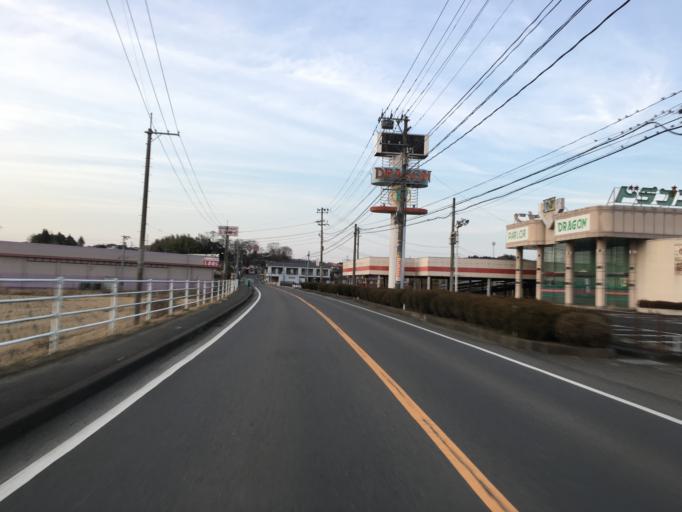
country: JP
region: Fukushima
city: Ishikawa
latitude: 37.0188
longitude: 140.3915
